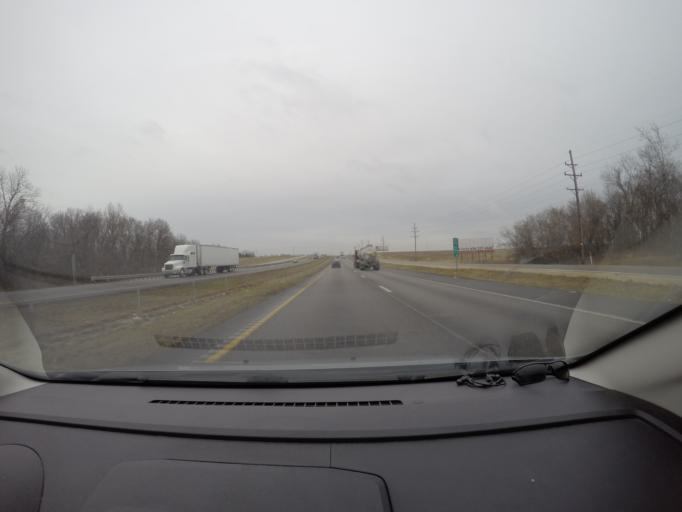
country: US
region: Missouri
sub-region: Warren County
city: Warrenton
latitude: 38.8460
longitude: -91.2594
